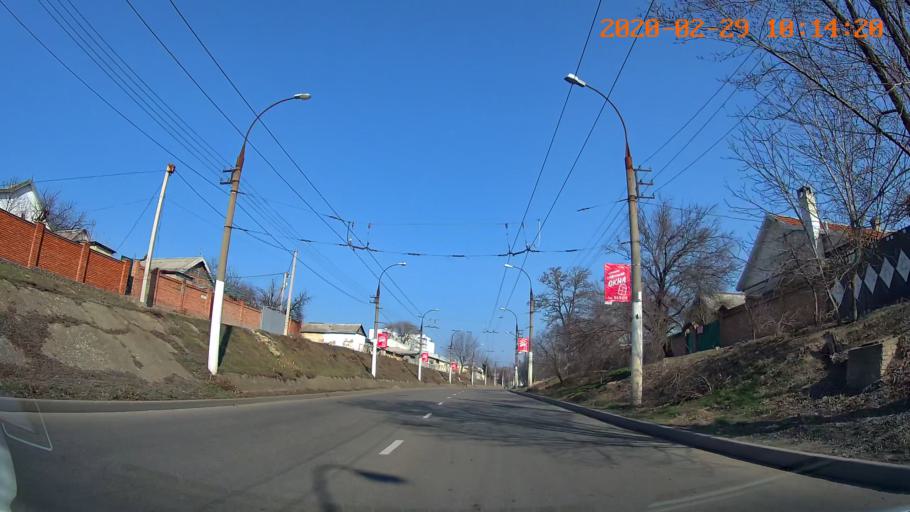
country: MD
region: Telenesti
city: Tiraspolul Nou
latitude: 46.8458
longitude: 29.6437
